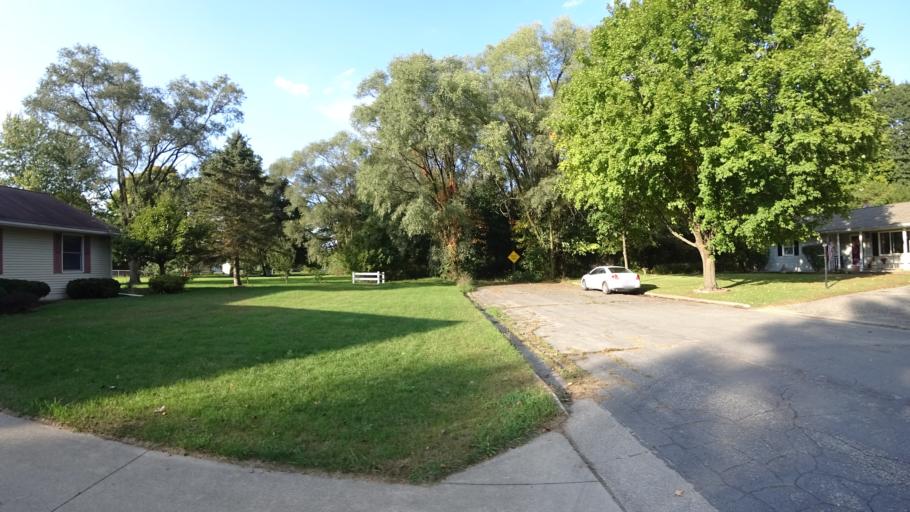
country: US
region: Michigan
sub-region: Saint Joseph County
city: Three Rivers
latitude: 41.9580
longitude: -85.6298
